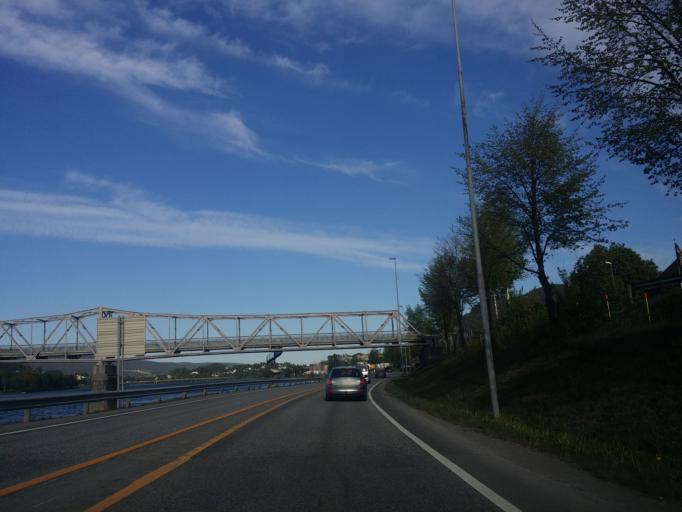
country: NO
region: Buskerud
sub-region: Nedre Eiker
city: Mjondalen
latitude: 59.7527
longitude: 10.0056
